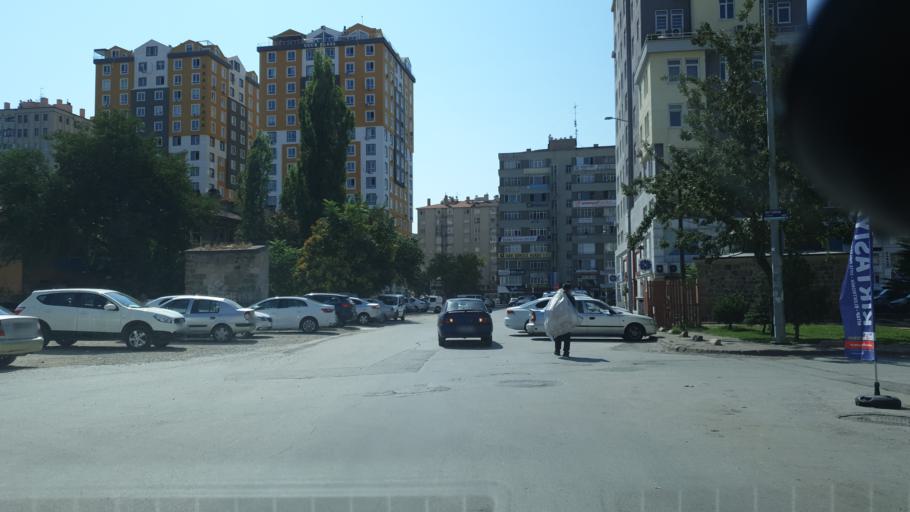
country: TR
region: Kayseri
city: Kayseri
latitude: 38.7257
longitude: 35.4918
